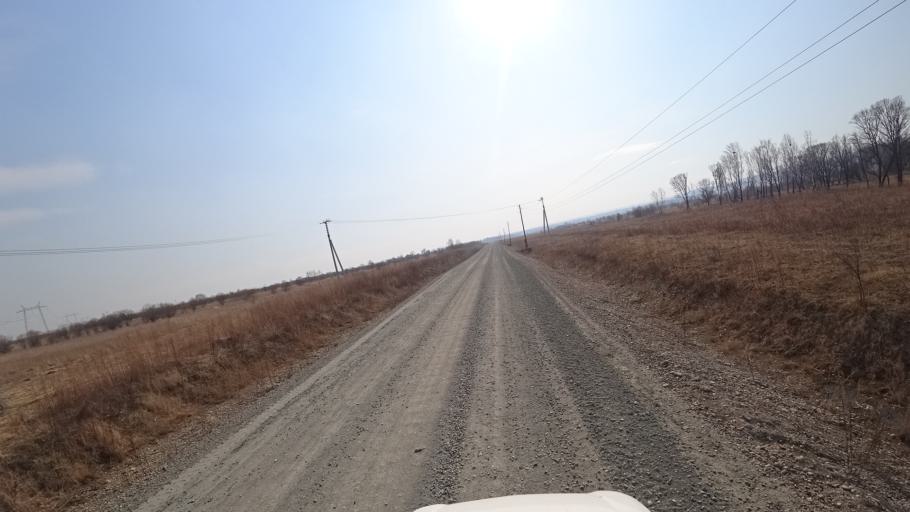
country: RU
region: Amur
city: Novobureyskiy
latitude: 49.8144
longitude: 129.9741
